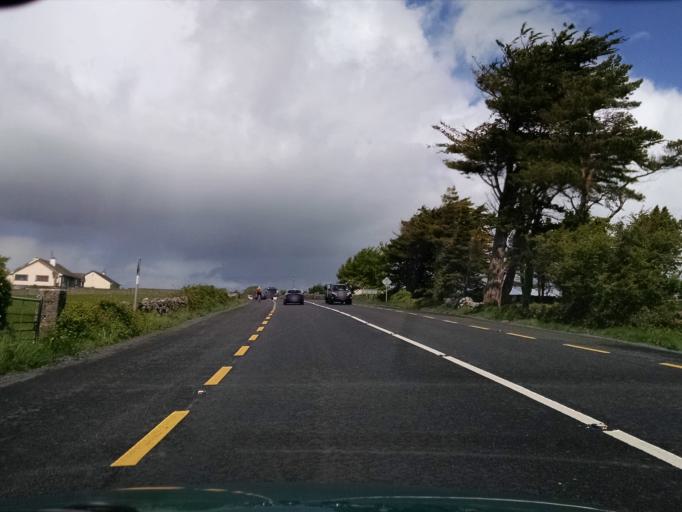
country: IE
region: Connaught
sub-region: County Galway
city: Oranmore
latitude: 53.2369
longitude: -8.8829
